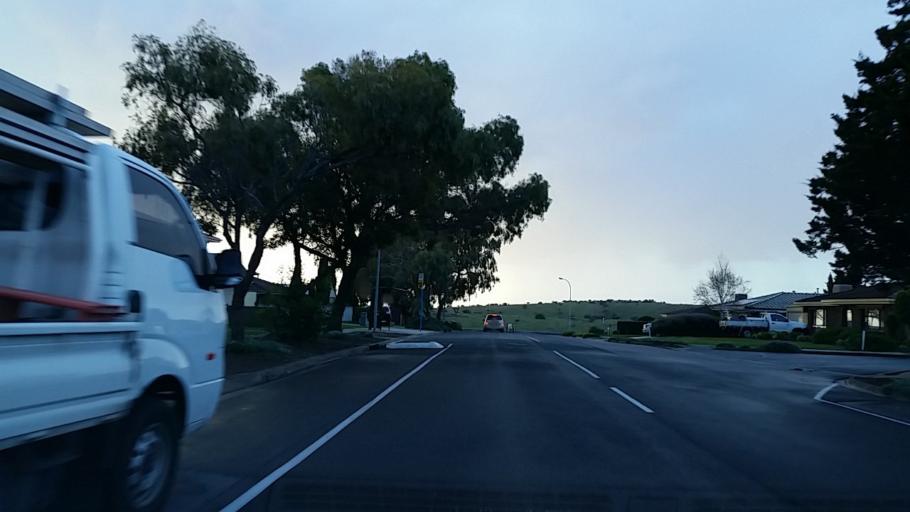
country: AU
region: South Australia
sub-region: Marion
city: Marino
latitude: -35.0636
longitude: 138.5163
